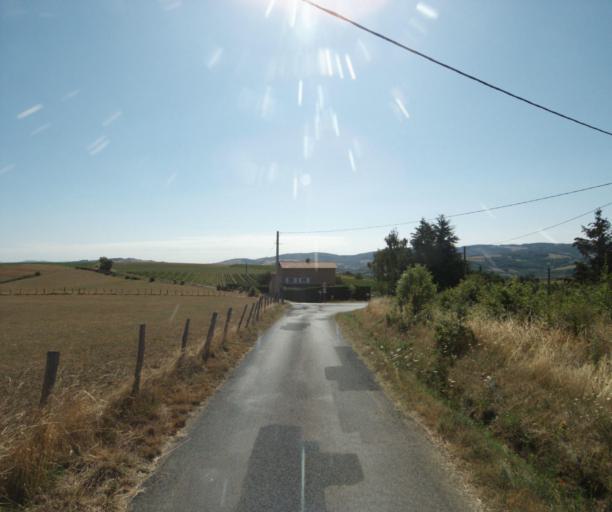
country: FR
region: Rhone-Alpes
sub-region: Departement du Rhone
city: Savigny
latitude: 45.8053
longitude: 4.5610
